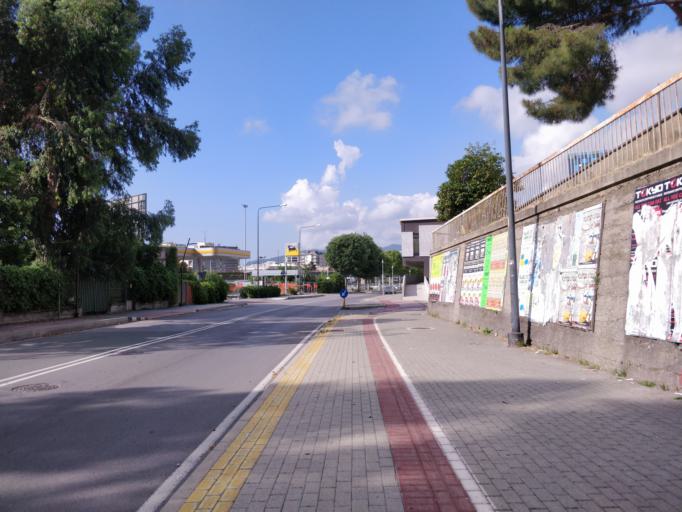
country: IT
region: Liguria
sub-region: Provincia di Savona
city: Savona
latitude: 44.3007
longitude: 8.4649
